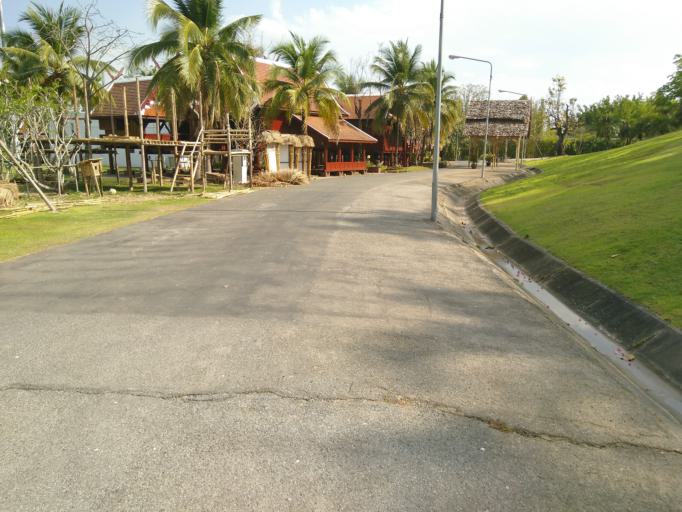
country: TH
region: Chiang Mai
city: Hang Dong
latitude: 18.7521
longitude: 98.9219
